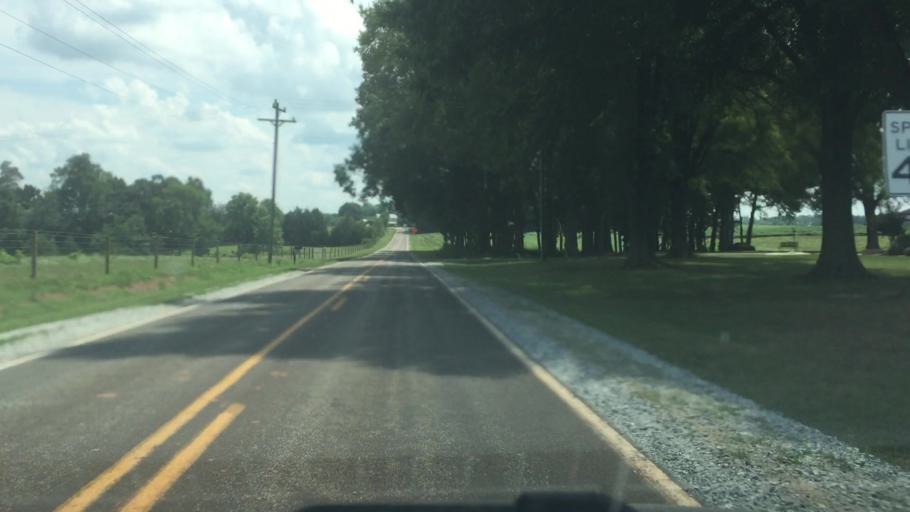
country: US
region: North Carolina
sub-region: Rowan County
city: Enochville
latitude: 35.6403
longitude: -80.6686
